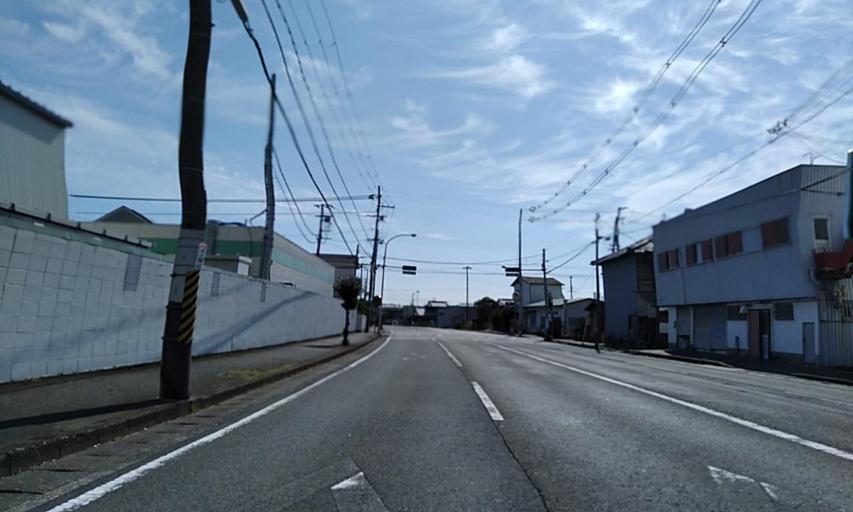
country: JP
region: Wakayama
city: Gobo
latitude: 33.8935
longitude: 135.1621
